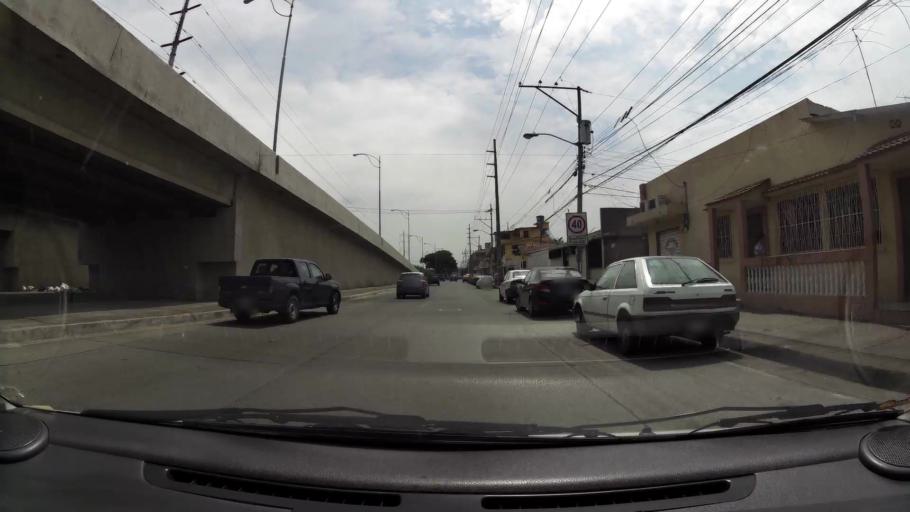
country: EC
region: Guayas
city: Eloy Alfaro
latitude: -2.1461
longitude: -79.9002
